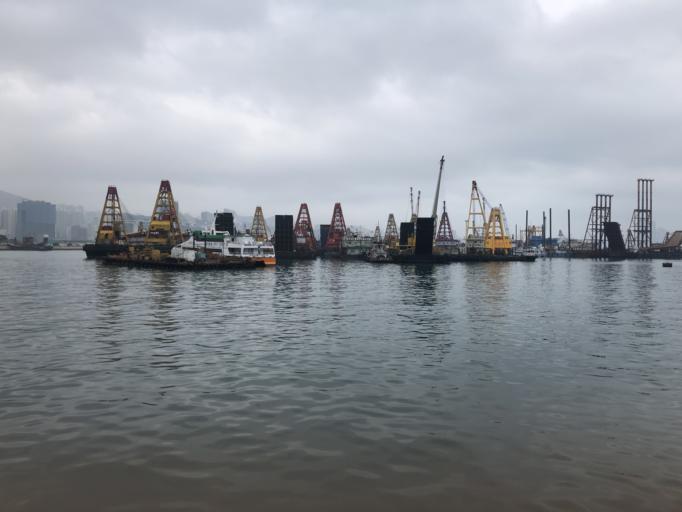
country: HK
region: Kowloon City
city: Kowloon
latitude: 22.3163
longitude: 114.1945
